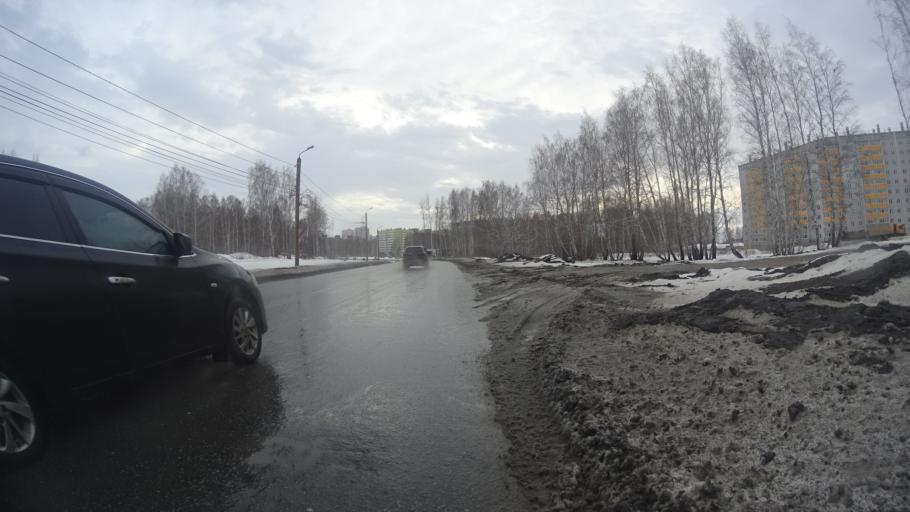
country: RU
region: Chelyabinsk
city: Roshchino
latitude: 55.2161
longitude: 61.2872
